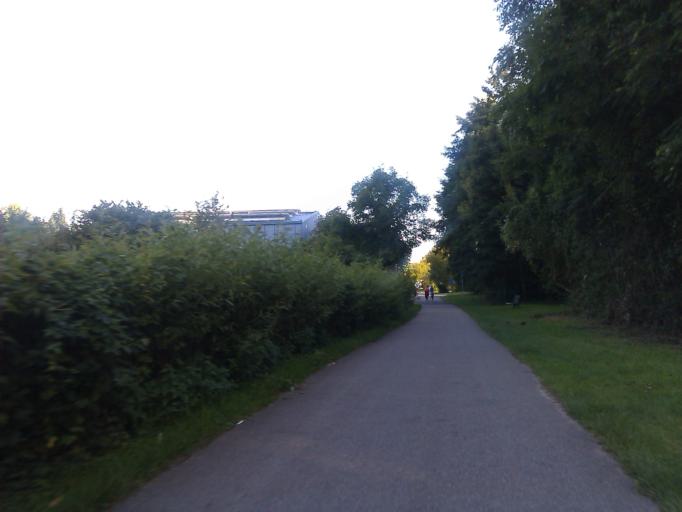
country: DE
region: Baden-Wuerttemberg
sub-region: Karlsruhe Region
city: Rauenberg
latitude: 49.2608
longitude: 8.7115
